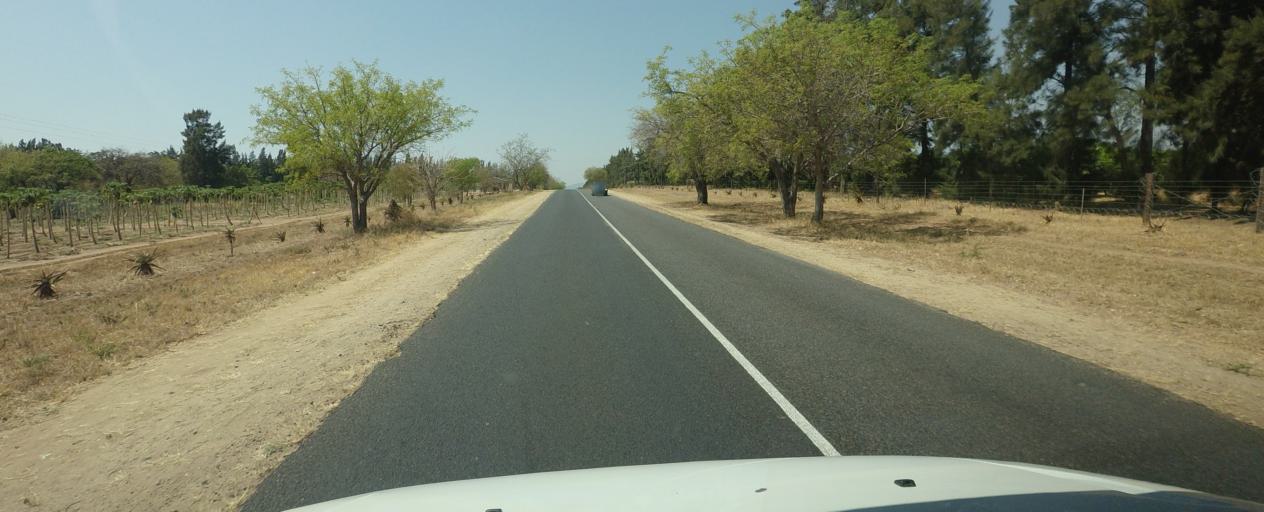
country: ZA
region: Limpopo
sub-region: Mopani District Municipality
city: Hoedspruit
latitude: -24.4322
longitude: 30.8467
